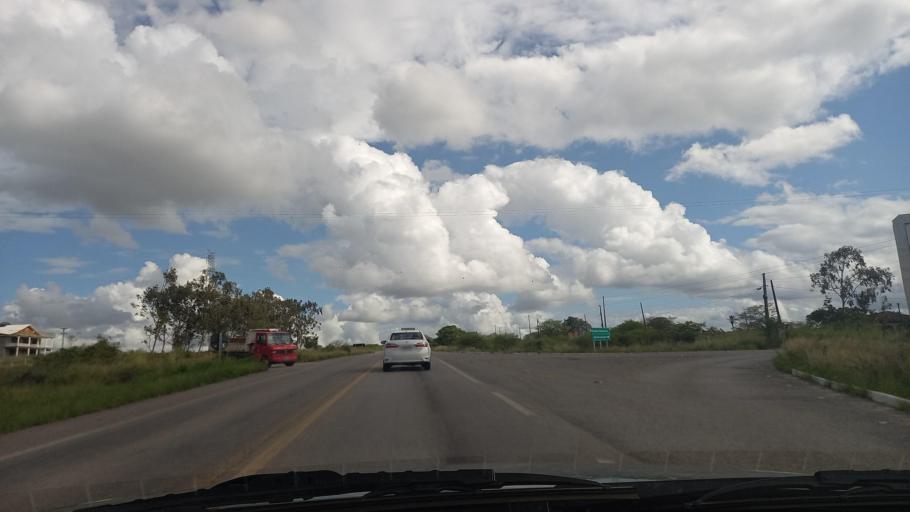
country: BR
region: Pernambuco
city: Garanhuns
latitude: -8.8318
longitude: -36.4536
